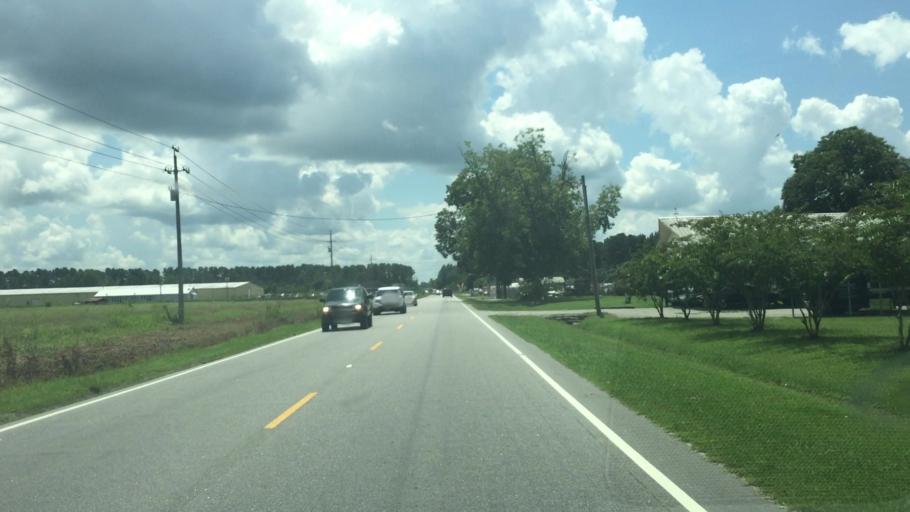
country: US
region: North Carolina
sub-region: Columbus County
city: Chadbourn
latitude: 34.3422
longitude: -78.8272
